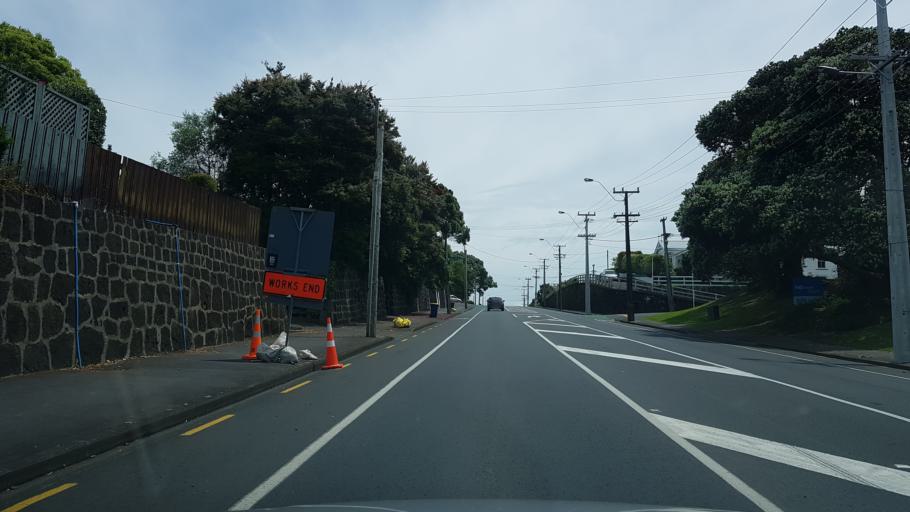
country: NZ
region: Auckland
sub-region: Auckland
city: North Shore
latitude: -36.8158
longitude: 174.7937
